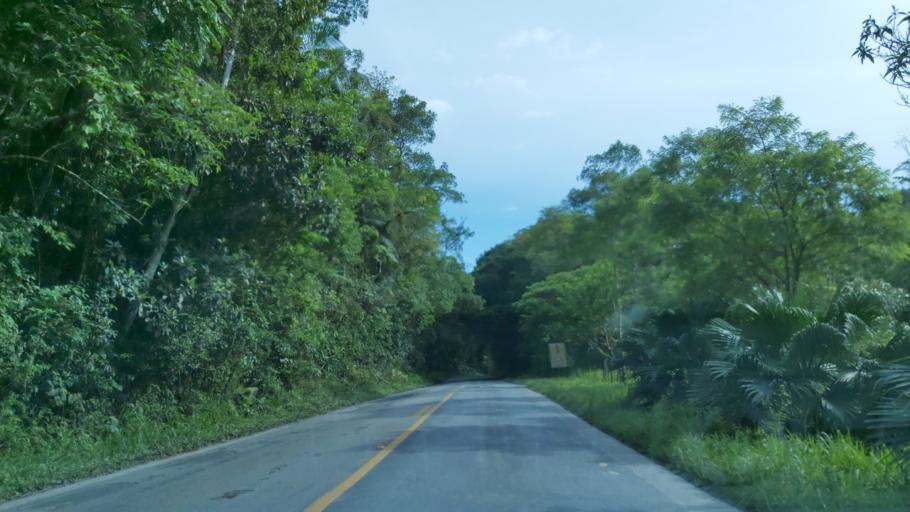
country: BR
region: Sao Paulo
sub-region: Miracatu
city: Miracatu
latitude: -24.0583
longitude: -47.5875
